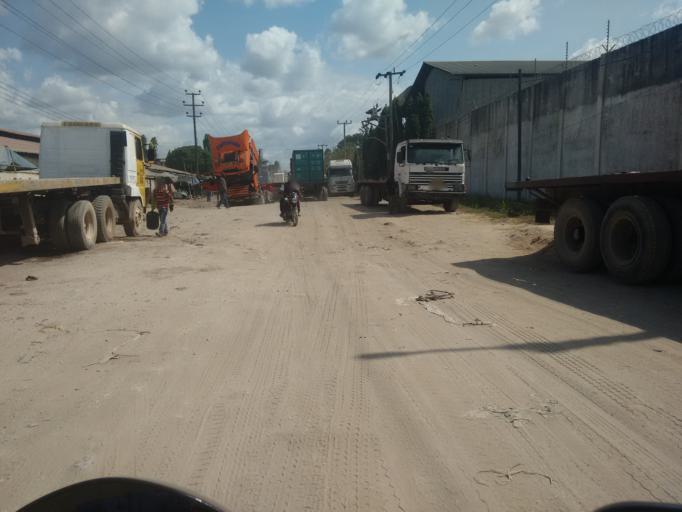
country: TZ
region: Dar es Salaam
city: Dar es Salaam
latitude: -6.8465
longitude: 39.2570
